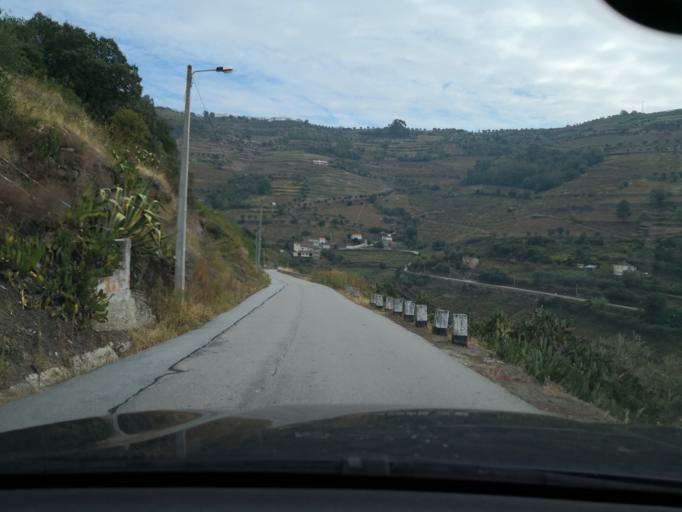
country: PT
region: Vila Real
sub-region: Peso da Regua
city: Peso da Regua
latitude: 41.1787
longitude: -7.7425
